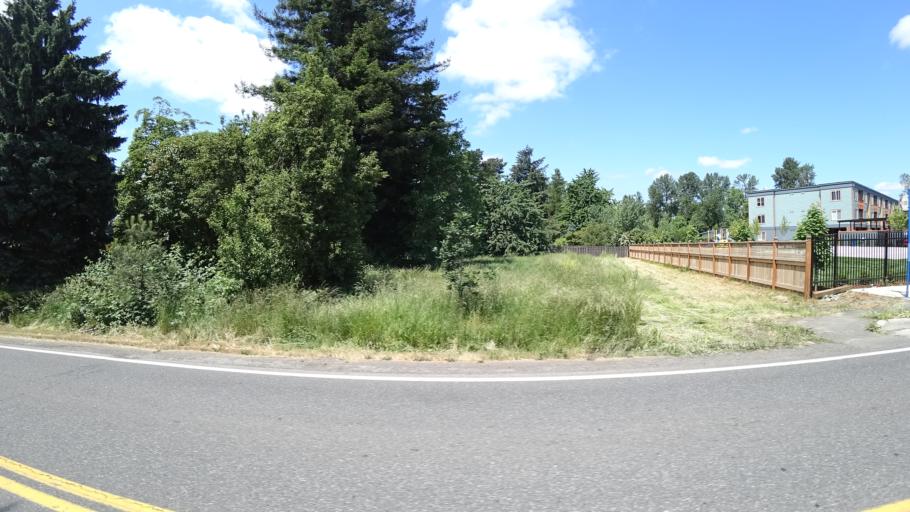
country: US
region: Washington
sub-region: Clark County
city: Vancouver
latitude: 45.5981
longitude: -122.6604
